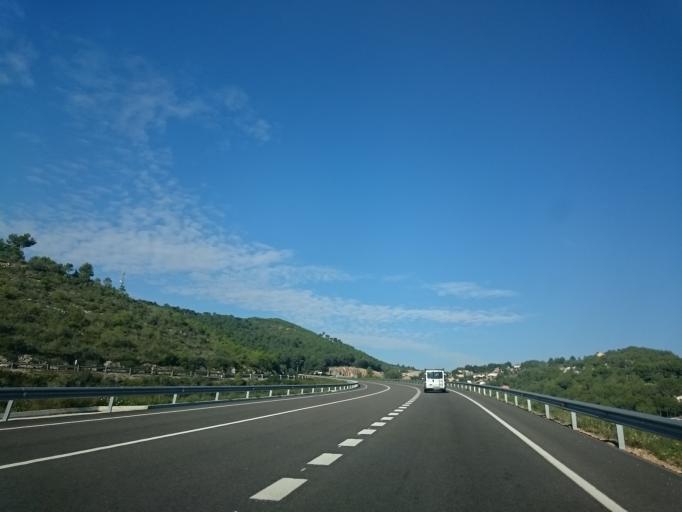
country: ES
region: Catalonia
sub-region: Provincia de Tarragona
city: la Bisbal del Penedes
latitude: 41.2753
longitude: 1.4414
